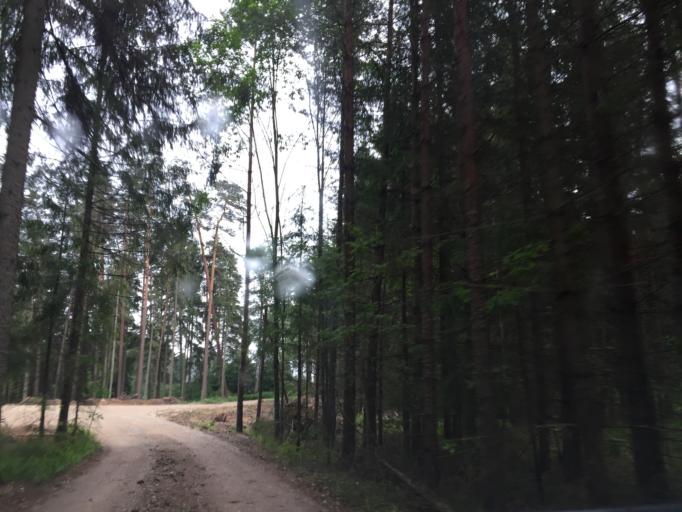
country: LV
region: Tukuma Rajons
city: Tukums
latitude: 57.0079
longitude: 23.0972
